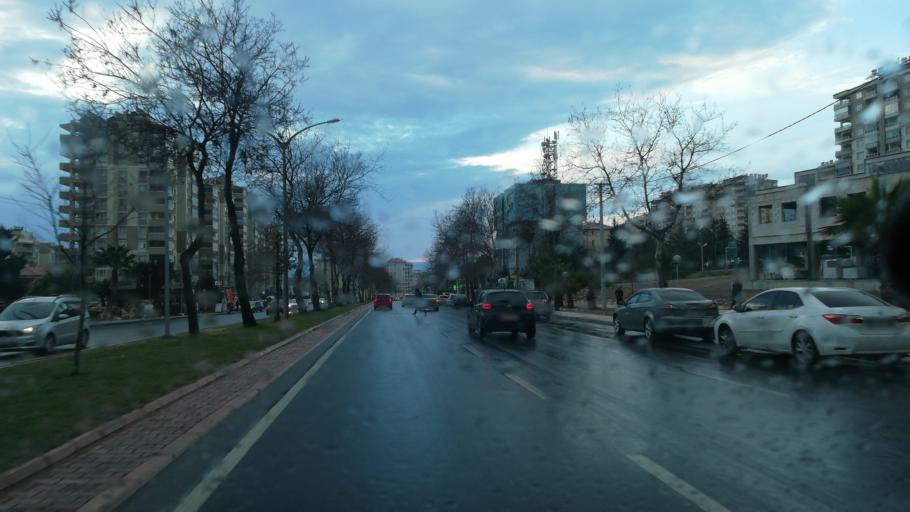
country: TR
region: Kahramanmaras
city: Kahramanmaras
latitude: 37.5889
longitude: 36.8826
